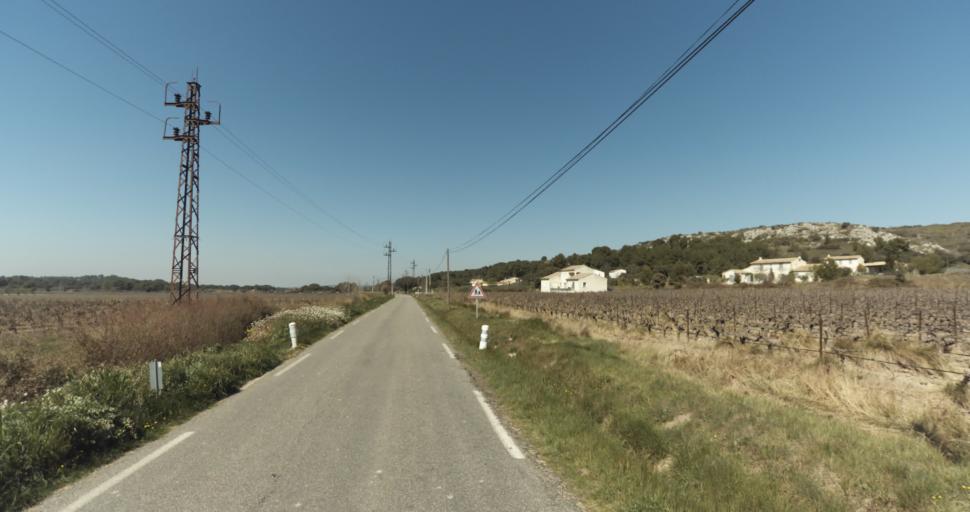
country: FR
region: Provence-Alpes-Cote d'Azur
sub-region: Departement des Bouches-du-Rhone
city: Pelissanne
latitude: 43.6066
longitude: 5.1858
